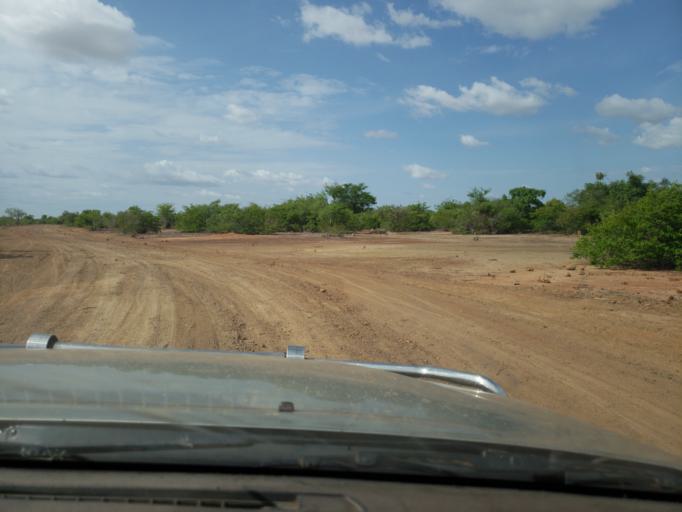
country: ML
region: Segou
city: Bla
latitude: 12.7784
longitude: -5.6092
